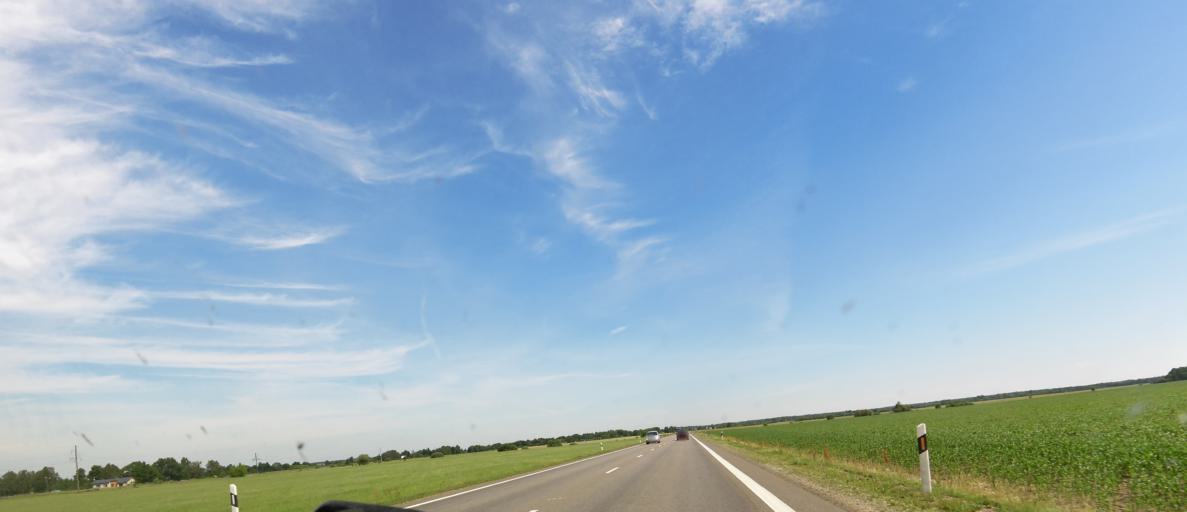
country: LT
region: Panevezys
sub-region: Panevezys City
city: Panevezys
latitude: 55.7843
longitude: 24.3090
